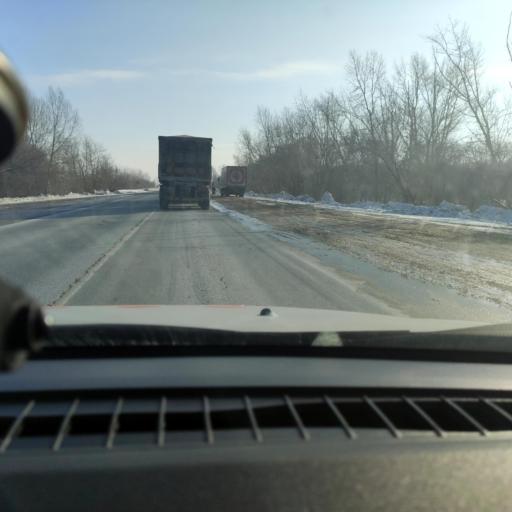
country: RU
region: Samara
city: Kinel'
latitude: 53.2044
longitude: 50.5086
